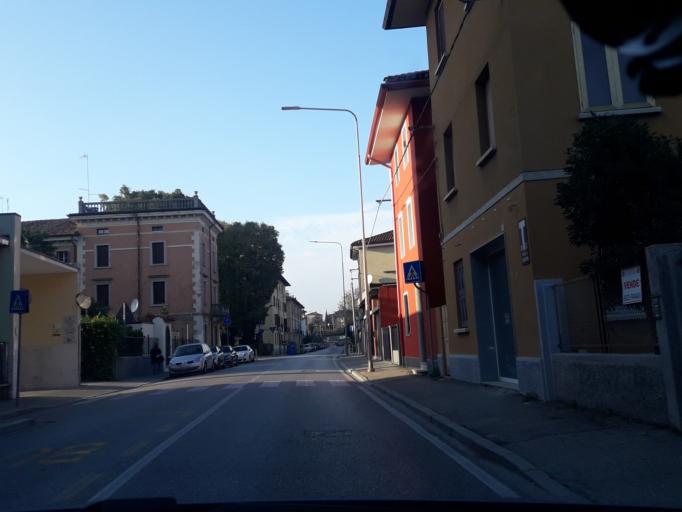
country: IT
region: Friuli Venezia Giulia
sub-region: Provincia di Udine
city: Udine
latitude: 46.0548
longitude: 13.2495
